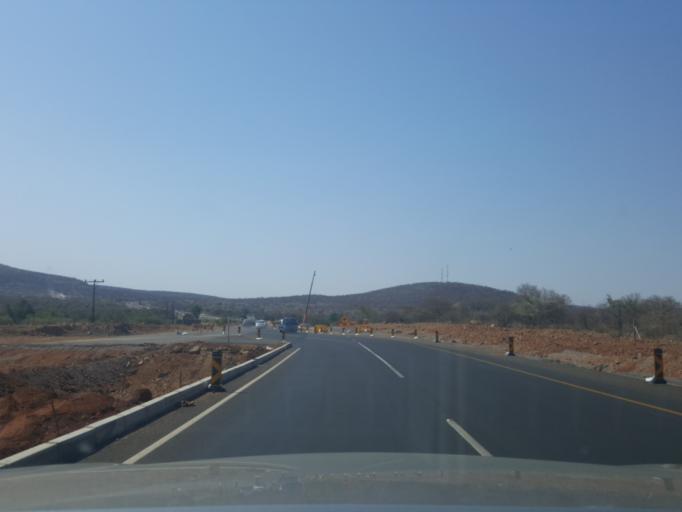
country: BW
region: Kweneng
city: Gabane
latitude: -24.7652
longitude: 25.8315
